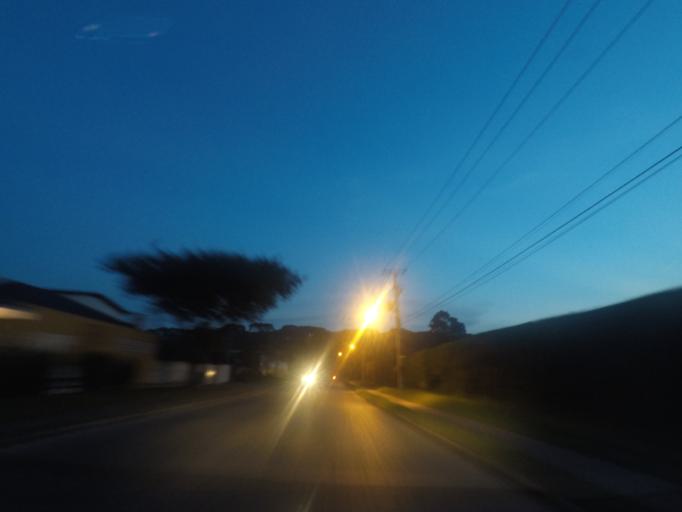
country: BR
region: Parana
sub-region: Pinhais
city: Pinhais
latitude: -25.4825
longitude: -49.1545
